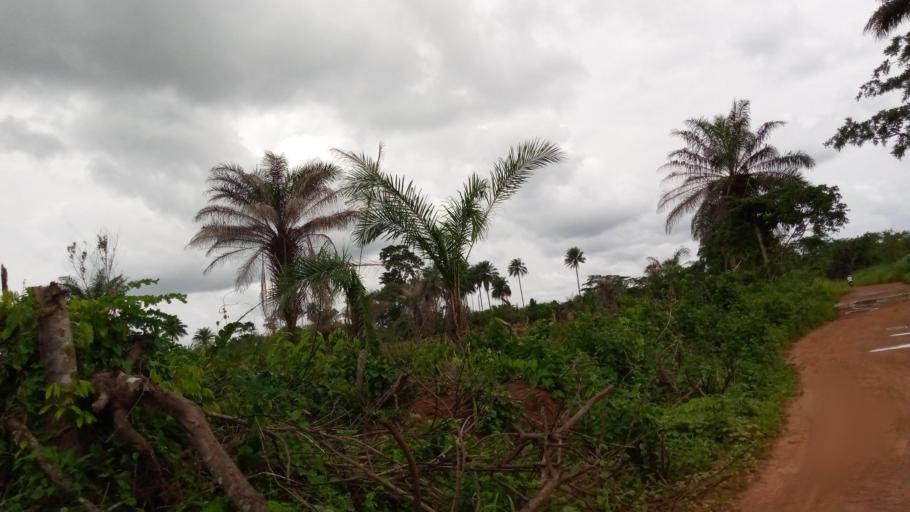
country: SL
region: Southern Province
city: Moyamba
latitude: 8.1956
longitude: -12.5444
